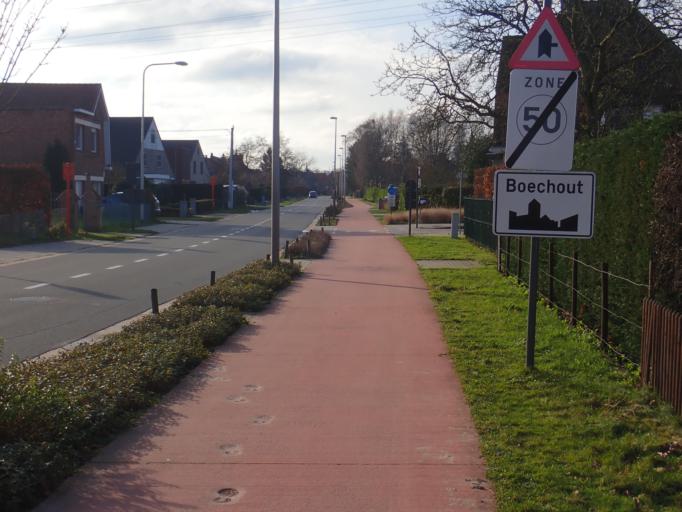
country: BE
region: Flanders
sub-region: Provincie Antwerpen
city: Boechout
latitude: 51.1701
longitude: 4.5127
